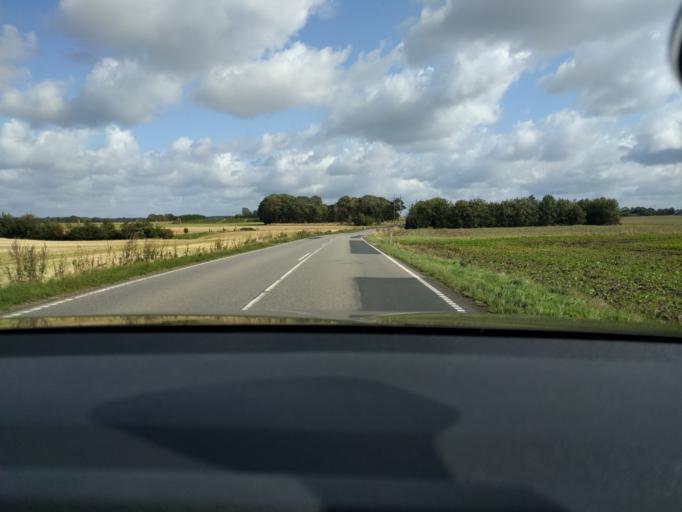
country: DK
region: Central Jutland
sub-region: Viborg Kommune
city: Bjerringbro
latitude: 56.3078
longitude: 9.7276
